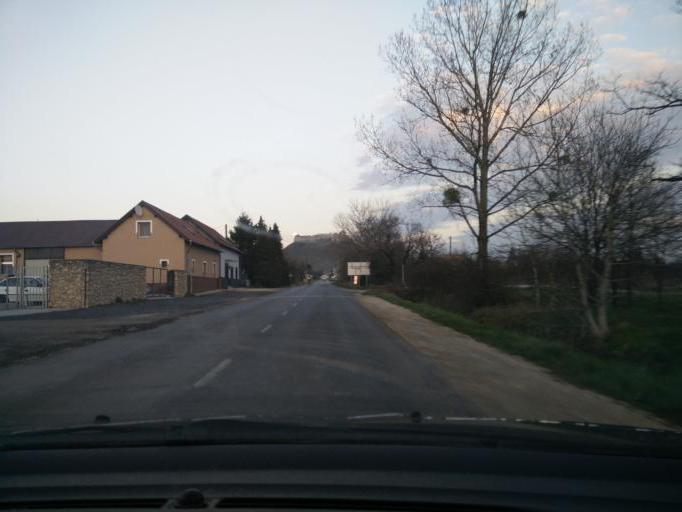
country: HU
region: Veszprem
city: Sumeg
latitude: 46.9833
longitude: 17.2674
